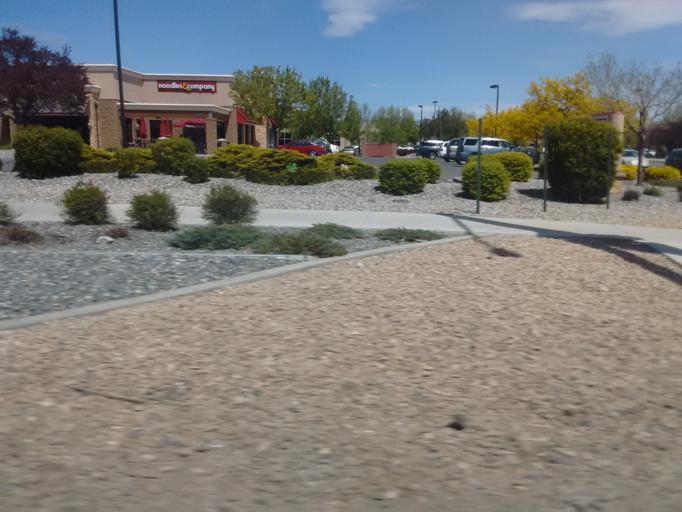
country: US
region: Colorado
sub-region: Mesa County
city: Redlands
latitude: 39.0852
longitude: -108.5943
